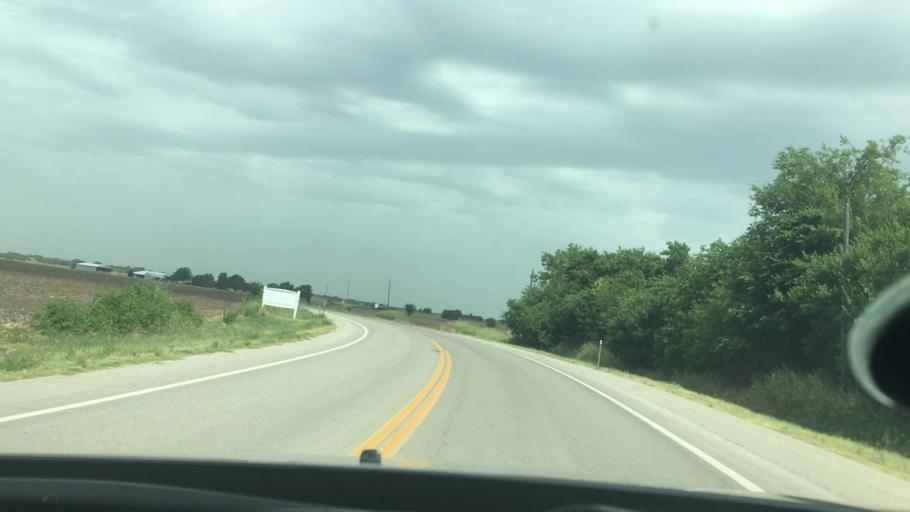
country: US
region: Oklahoma
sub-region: Garvin County
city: Pauls Valley
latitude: 34.8300
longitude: -97.2597
